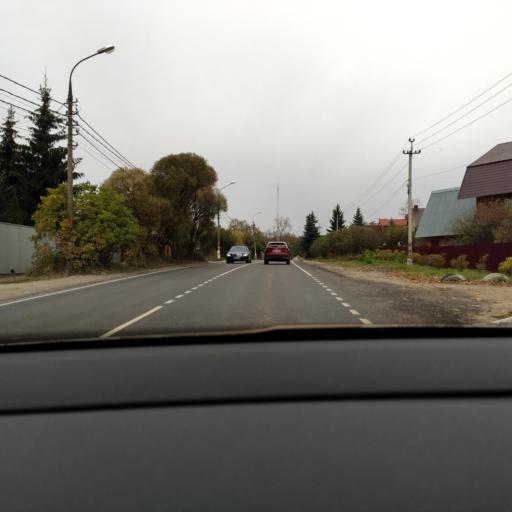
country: RU
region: Moskovskaya
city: Ivanteyevka
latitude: 55.9833
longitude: 37.9319
